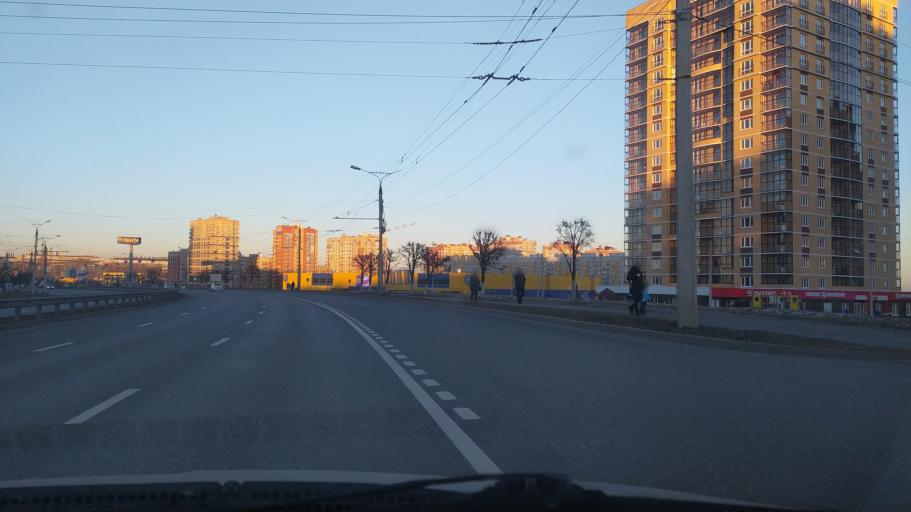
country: RU
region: Chuvashia
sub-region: Cheboksarskiy Rayon
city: Cheboksary
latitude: 56.1072
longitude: 47.3261
